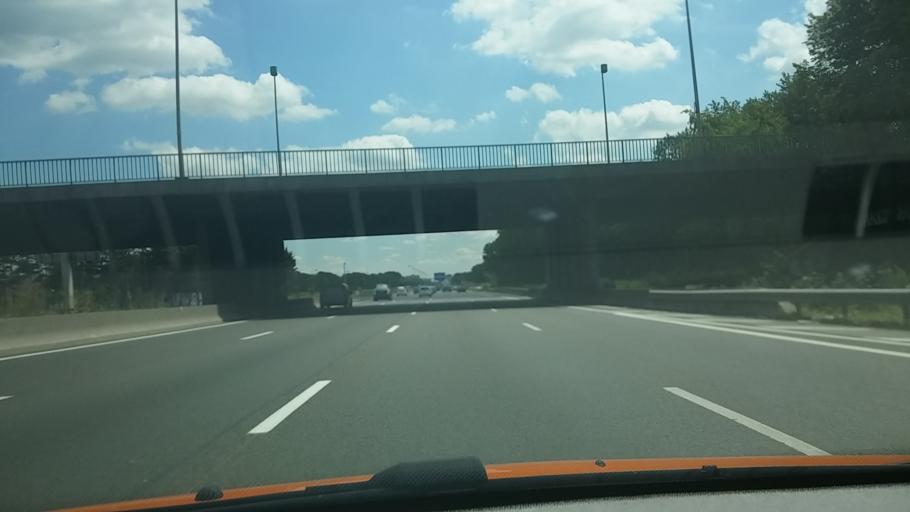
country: FR
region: Ile-de-France
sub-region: Departement de Seine-Saint-Denis
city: Noisy-le-Grand
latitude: 48.8358
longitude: 2.5619
